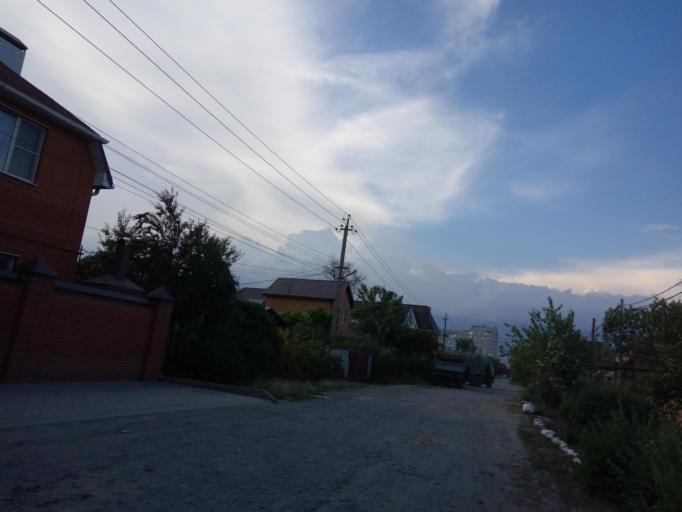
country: RU
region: Rostov
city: Bataysk
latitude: 47.1182
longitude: 39.7358
